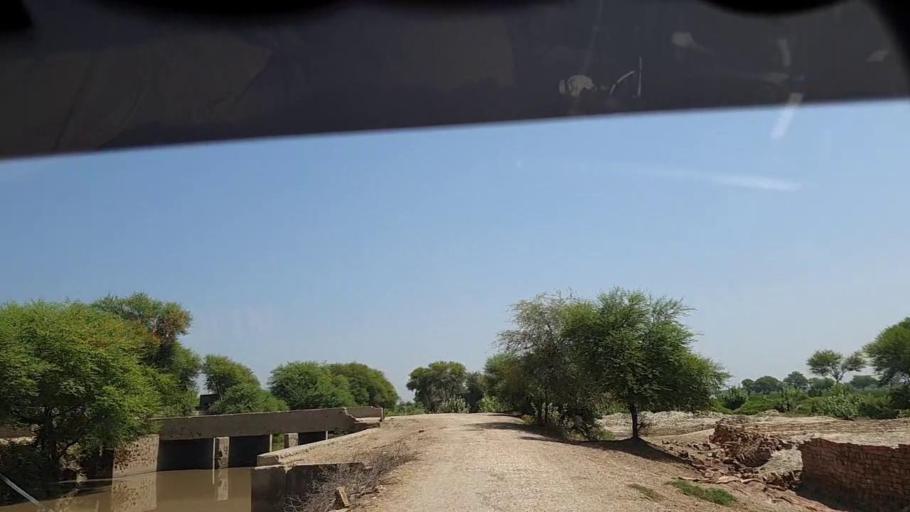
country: PK
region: Sindh
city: Ghauspur
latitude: 28.1687
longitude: 69.0698
